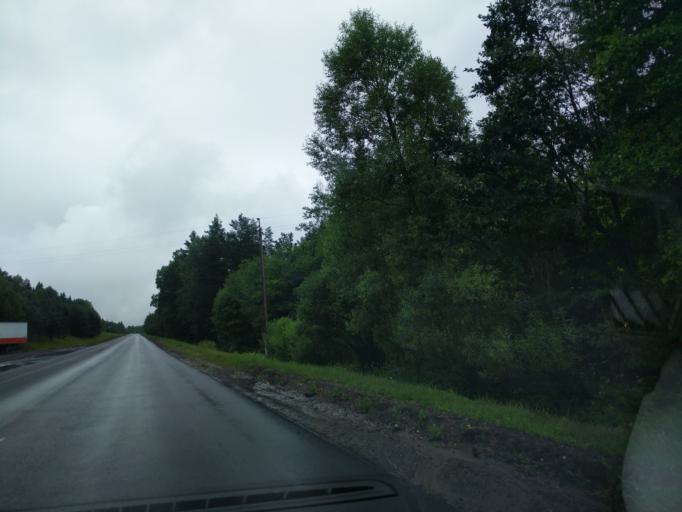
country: BY
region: Minsk
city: Syomkava
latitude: 54.2393
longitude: 27.4852
